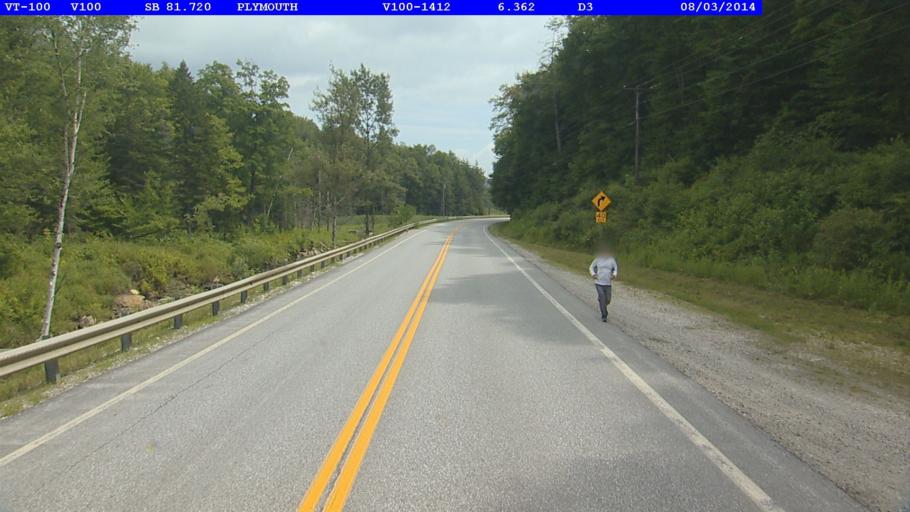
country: US
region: Vermont
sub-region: Rutland County
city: Rutland
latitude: 43.5427
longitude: -72.7493
